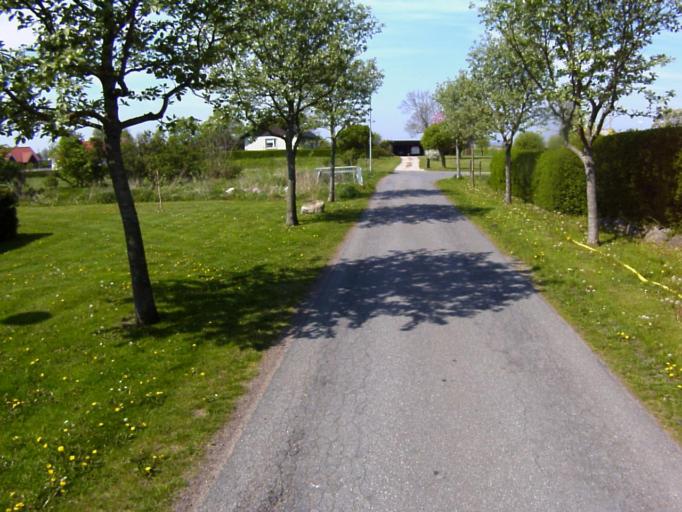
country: SE
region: Skane
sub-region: Kristianstads Kommun
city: Ahus
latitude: 55.9819
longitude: 14.2682
